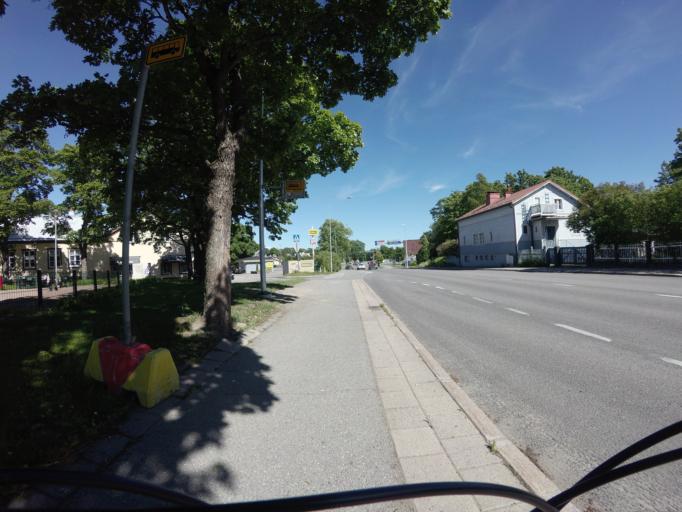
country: FI
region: Varsinais-Suomi
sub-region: Turku
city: Turku
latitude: 60.4598
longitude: 22.2638
